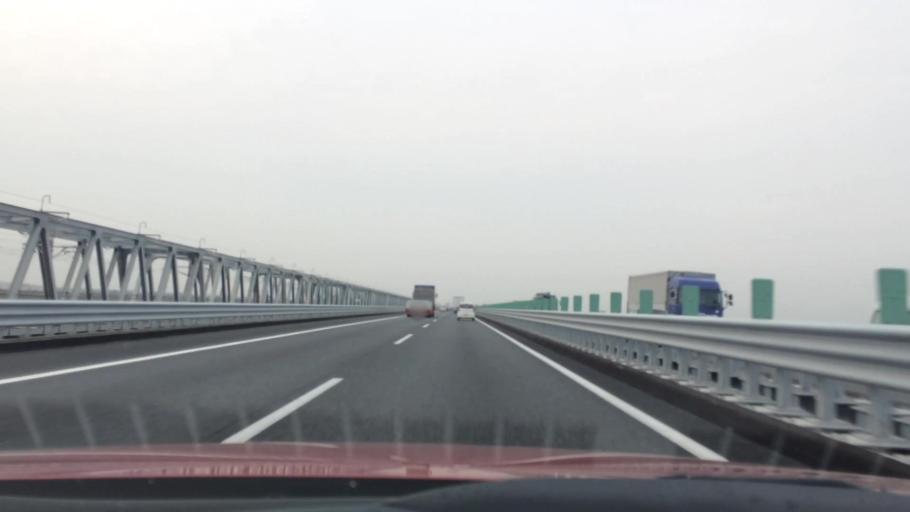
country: JP
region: Aichi
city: Sobue
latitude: 35.2944
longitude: 136.7274
